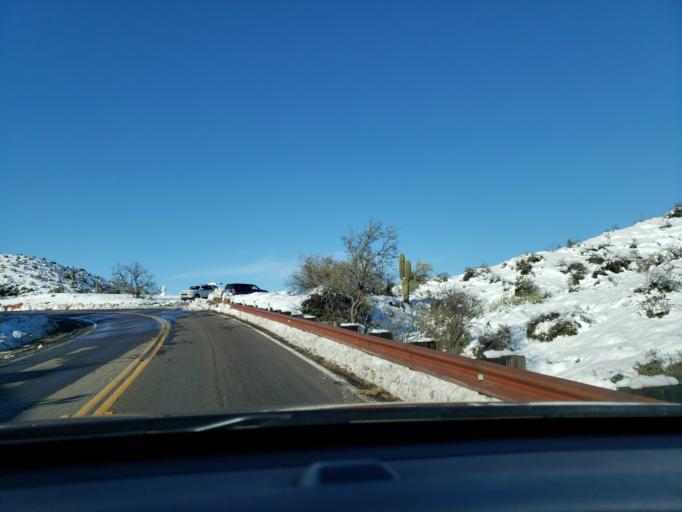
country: US
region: Arizona
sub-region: Maricopa County
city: Carefree
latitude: 33.8923
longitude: -111.8197
